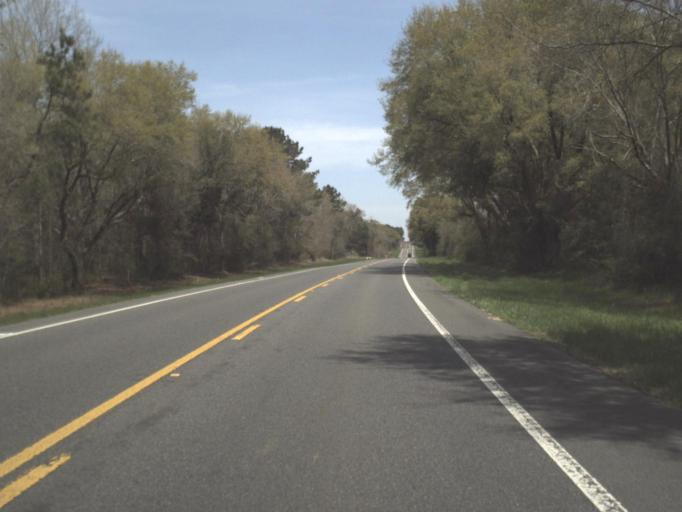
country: US
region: Florida
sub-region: Walton County
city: DeFuniak Springs
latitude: 30.8220
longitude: -85.9576
